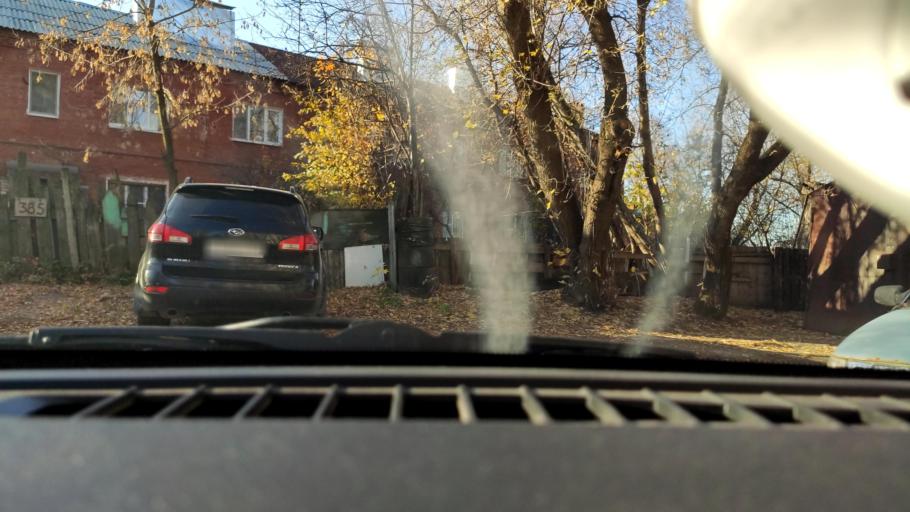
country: RU
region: Perm
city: Perm
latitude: 57.9607
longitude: 56.2297
